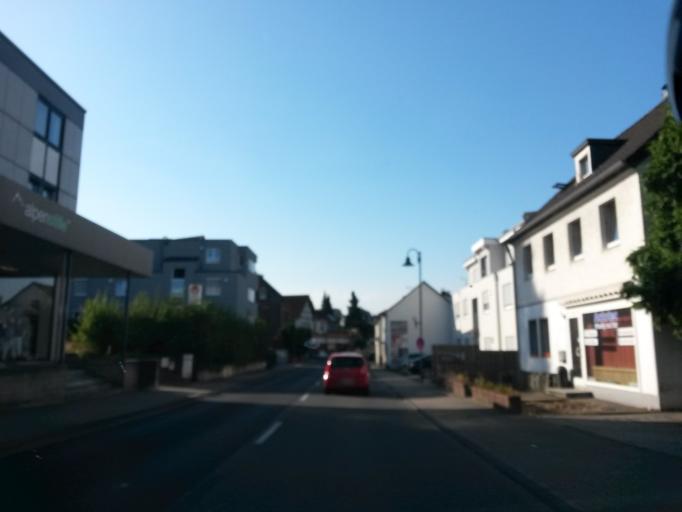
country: DE
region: North Rhine-Westphalia
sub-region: Regierungsbezirk Koln
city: Rosrath
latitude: 50.9275
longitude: 7.1767
